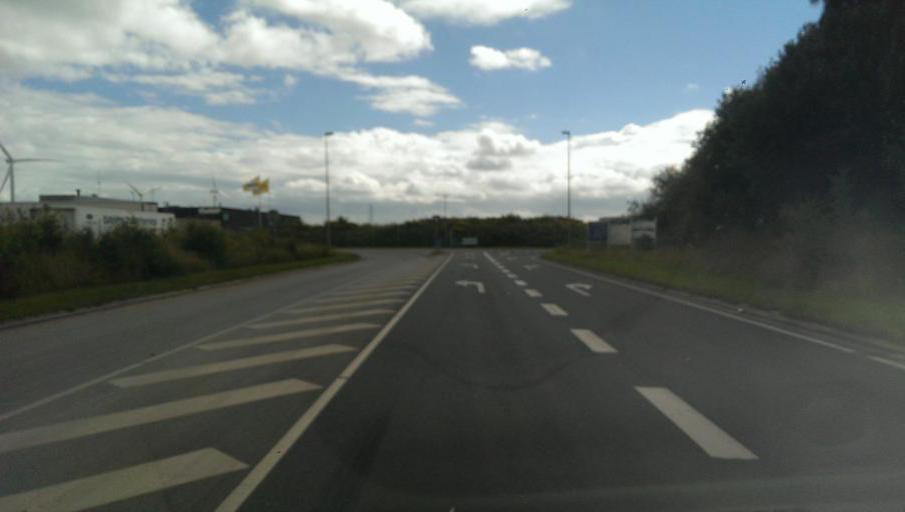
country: DK
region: South Denmark
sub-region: Esbjerg Kommune
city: Esbjerg
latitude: 55.4610
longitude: 8.4963
